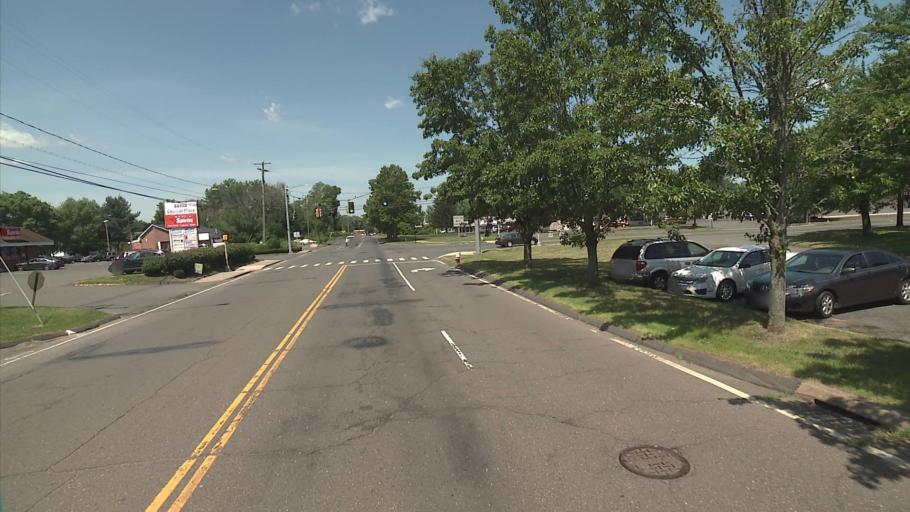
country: US
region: Connecticut
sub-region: Hartford County
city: Kensington
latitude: 41.6260
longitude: -72.7487
